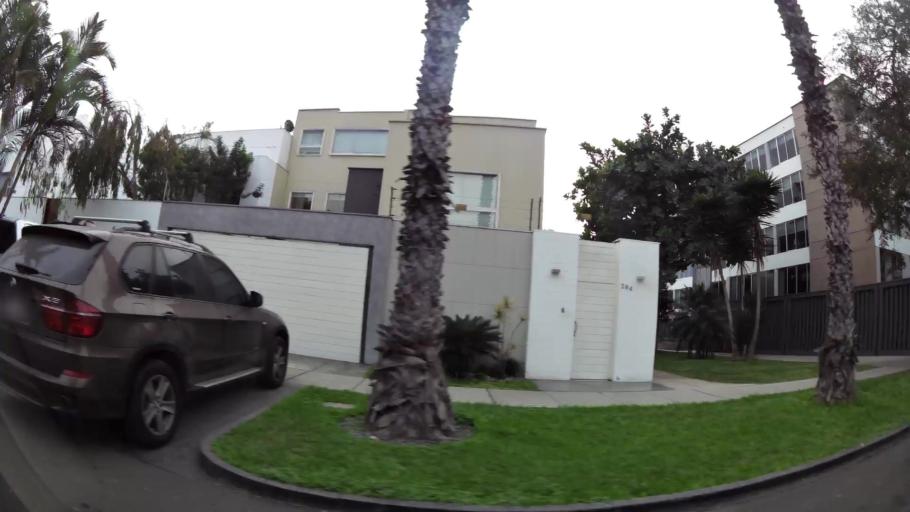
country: PE
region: Lima
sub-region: Lima
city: San Isidro
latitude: -12.1051
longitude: -77.0492
